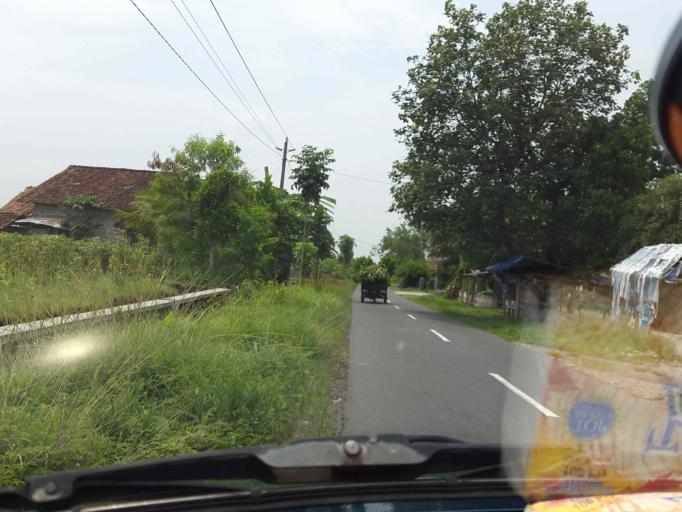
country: ID
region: Daerah Istimewa Yogyakarta
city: Sleman
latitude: -7.6810
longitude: 110.2731
